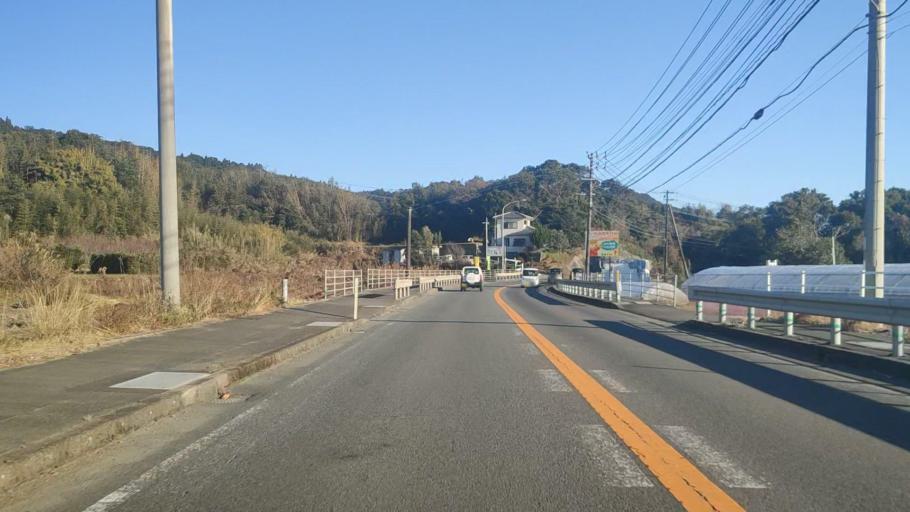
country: JP
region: Miyazaki
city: Nobeoka
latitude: 32.3636
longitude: 131.6232
